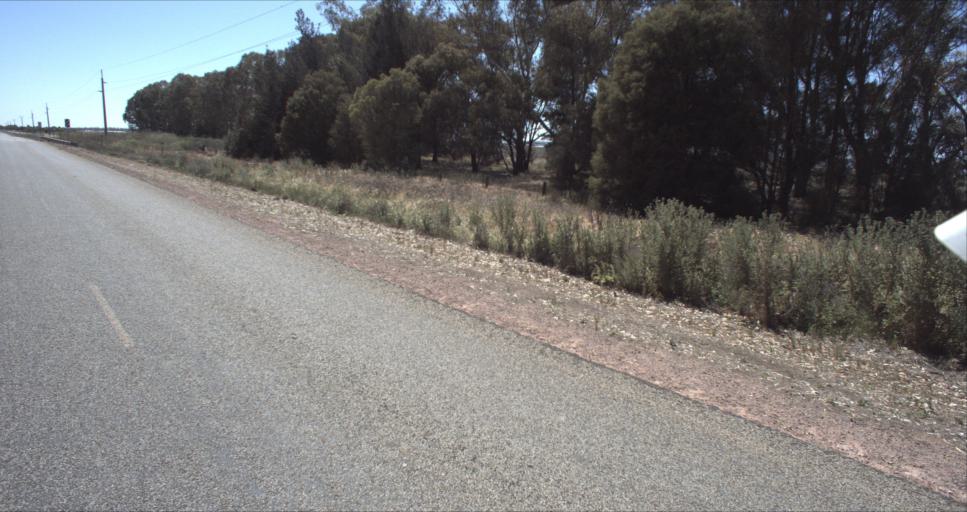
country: AU
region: New South Wales
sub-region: Leeton
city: Leeton
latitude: -34.4657
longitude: 146.2933
